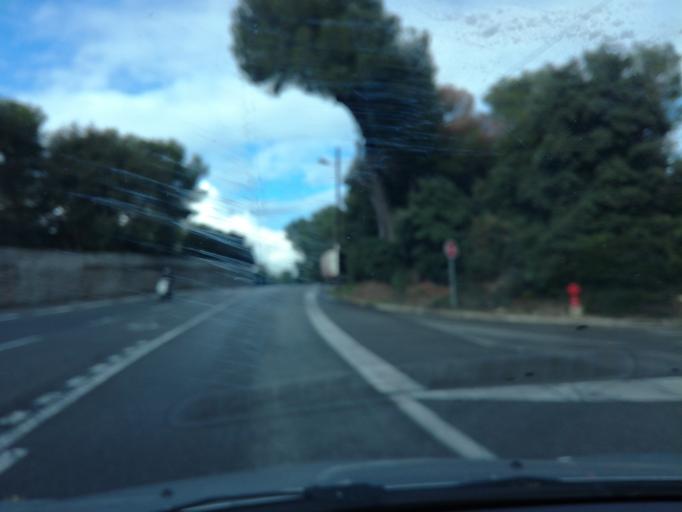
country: FR
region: Provence-Alpes-Cote d'Azur
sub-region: Departement des Alpes-Maritimes
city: Pegomas
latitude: 43.6242
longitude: 6.9353
